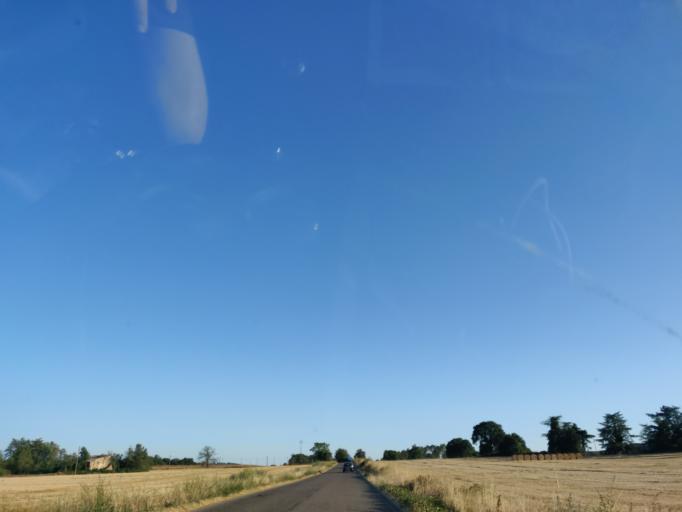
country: IT
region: Latium
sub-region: Provincia di Viterbo
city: Acquapendente
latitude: 42.7138
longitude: 11.8772
